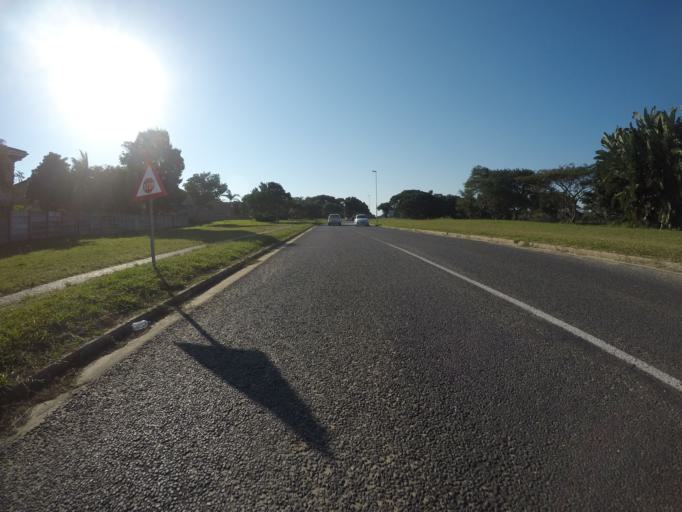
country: ZA
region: KwaZulu-Natal
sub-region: uThungulu District Municipality
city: Richards Bay
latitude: -28.7915
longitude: 32.0982
